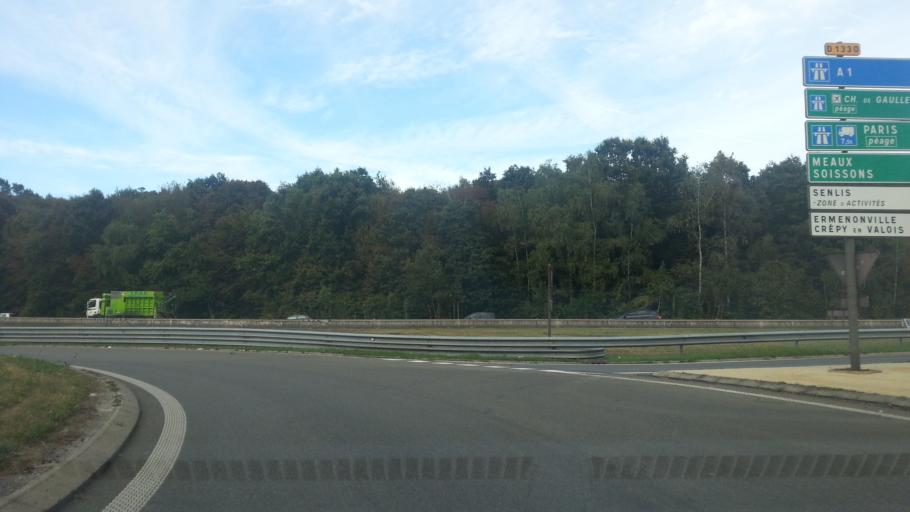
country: FR
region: Picardie
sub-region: Departement de l'Oise
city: Avilly-Saint-Leonard
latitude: 49.2167
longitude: 2.5560
